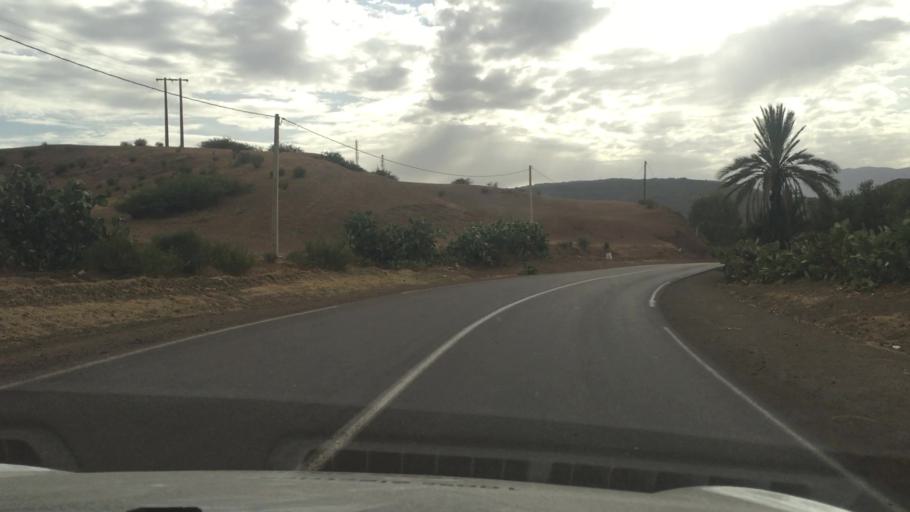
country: MA
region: Marrakech-Tensift-Al Haouz
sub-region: Al-Haouz
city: Touama
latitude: 31.5496
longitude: -7.5775
